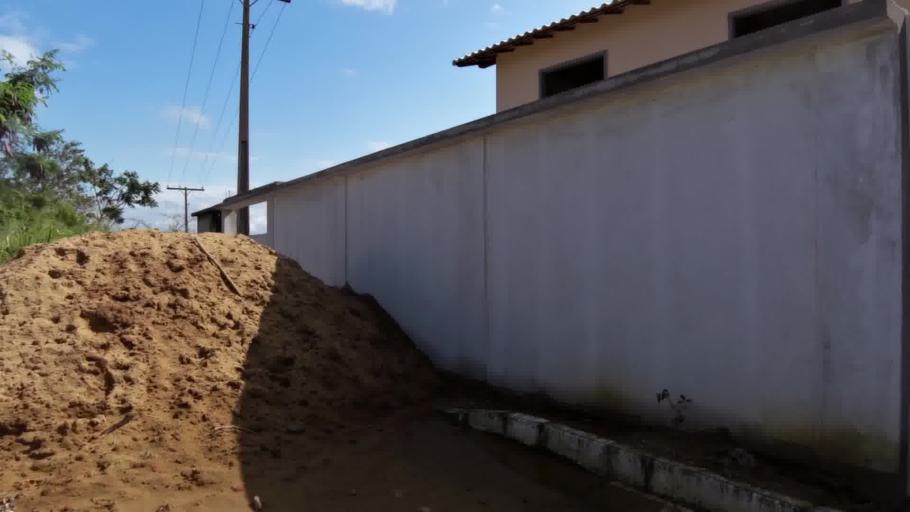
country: BR
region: Espirito Santo
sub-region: Piuma
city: Piuma
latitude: -20.8207
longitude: -40.6831
